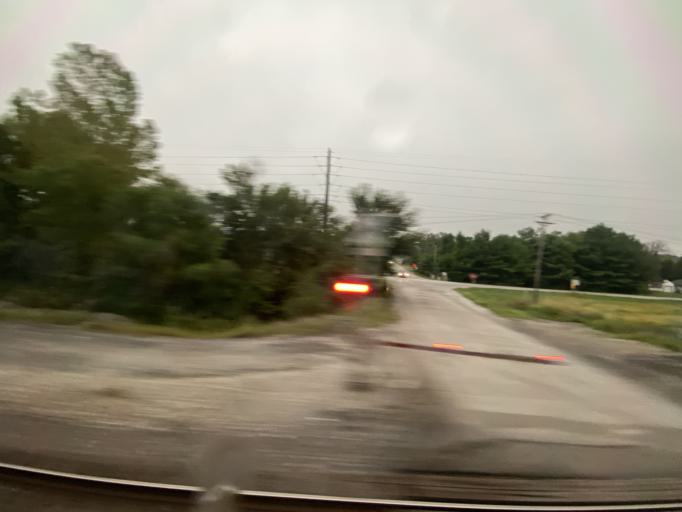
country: US
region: Iowa
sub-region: Lee County
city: Fort Madison
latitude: 40.6190
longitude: -91.2816
